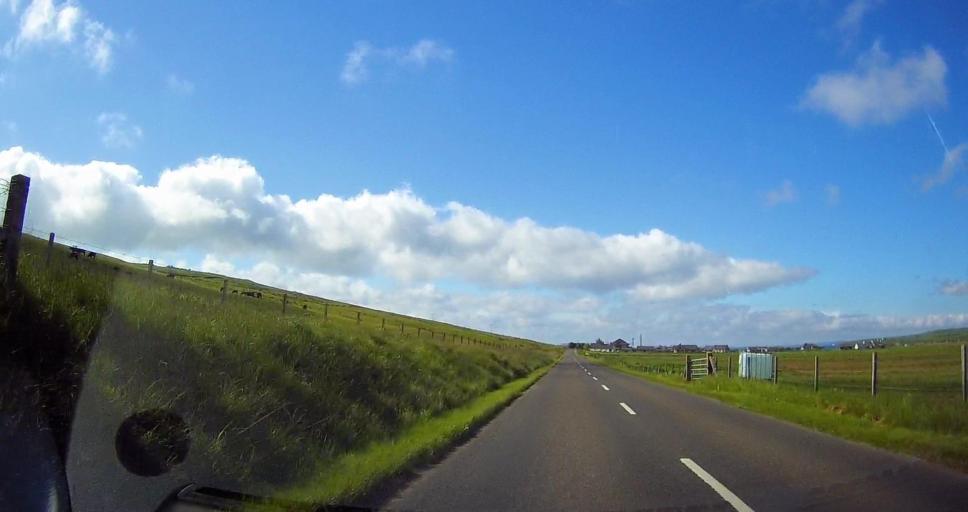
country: GB
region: Scotland
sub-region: Orkney Islands
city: Orkney
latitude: 58.9669
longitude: -2.9646
